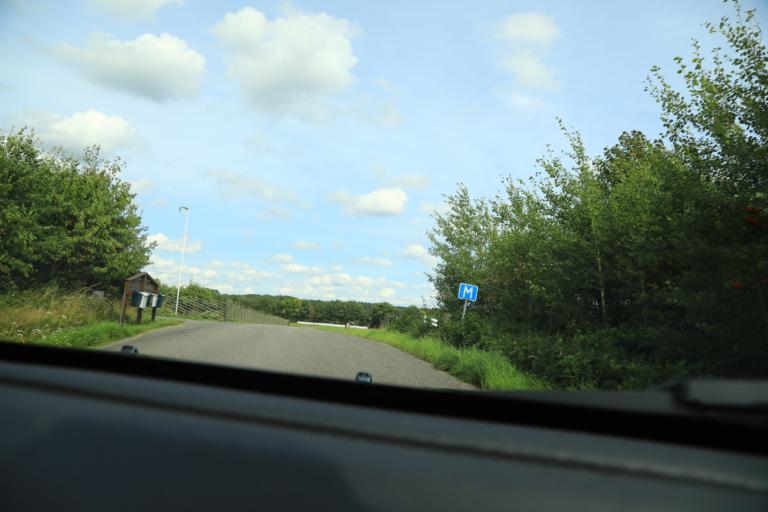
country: SE
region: Halland
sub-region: Varbergs Kommun
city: Varberg
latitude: 57.1733
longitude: 12.2452
